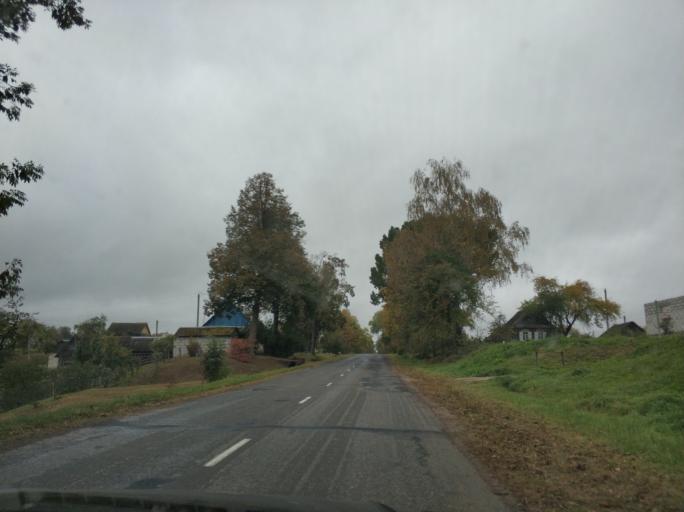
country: BY
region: Vitebsk
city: Polatsk
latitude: 55.4296
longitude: 29.0004
